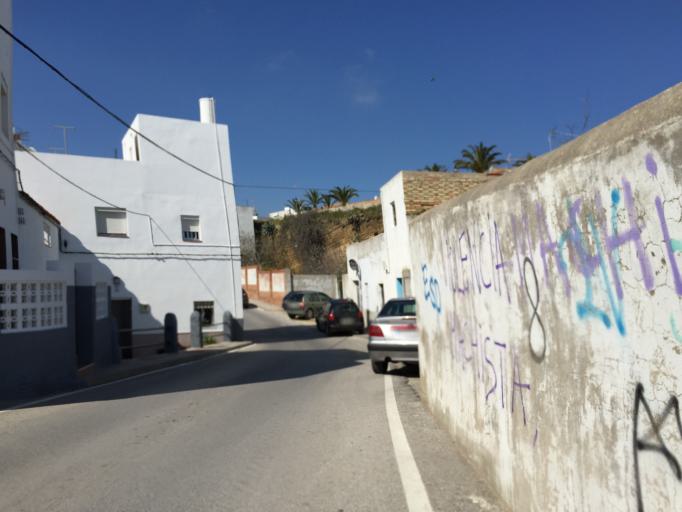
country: ES
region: Andalusia
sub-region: Provincia de Cadiz
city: Conil de la Frontera
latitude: 36.2769
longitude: -6.0856
